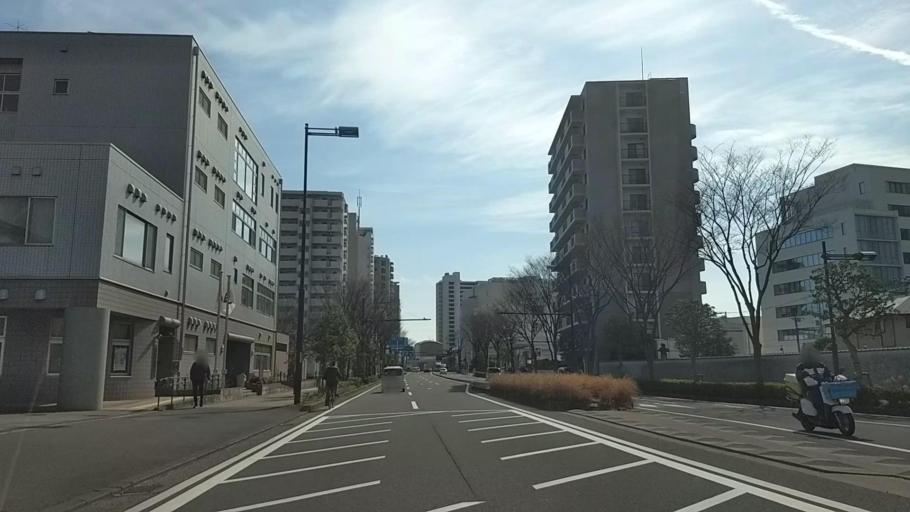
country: JP
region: Kanagawa
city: Fujisawa
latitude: 35.3408
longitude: 139.4492
